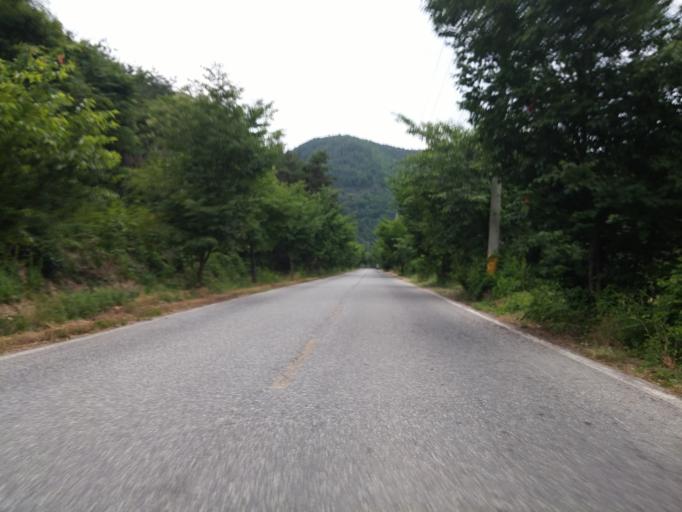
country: KR
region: Chungcheongbuk-do
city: Okcheon
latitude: 36.2011
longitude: 127.5682
